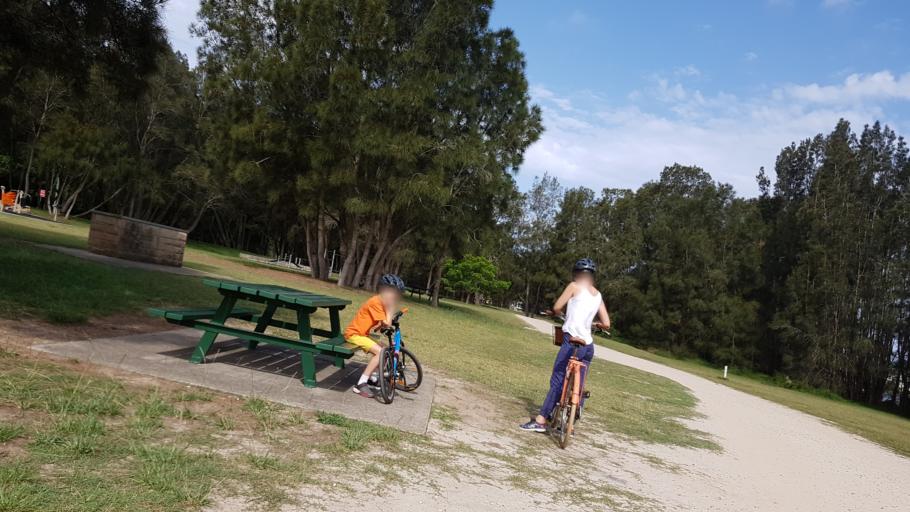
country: AU
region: New South Wales
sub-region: Pittwater
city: North Narrabeen
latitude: -33.7110
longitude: 151.2891
